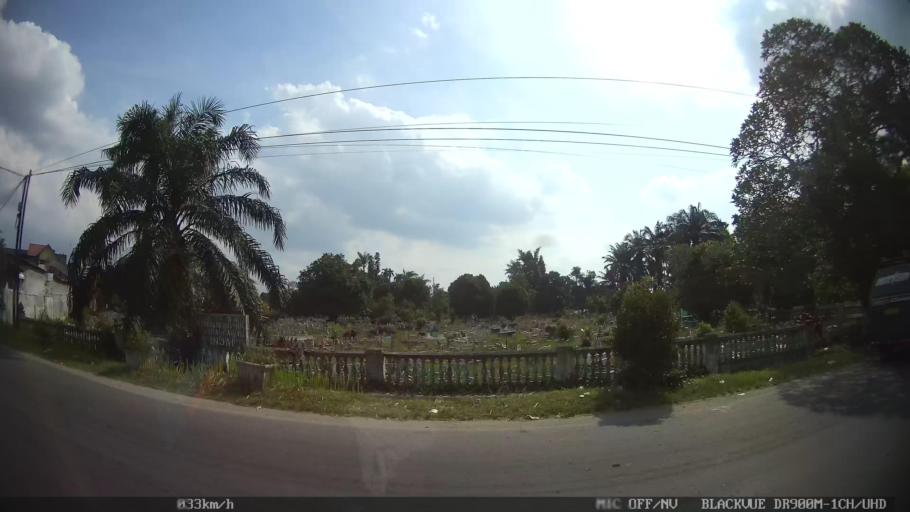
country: ID
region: North Sumatra
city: Binjai
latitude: 3.6272
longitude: 98.4942
